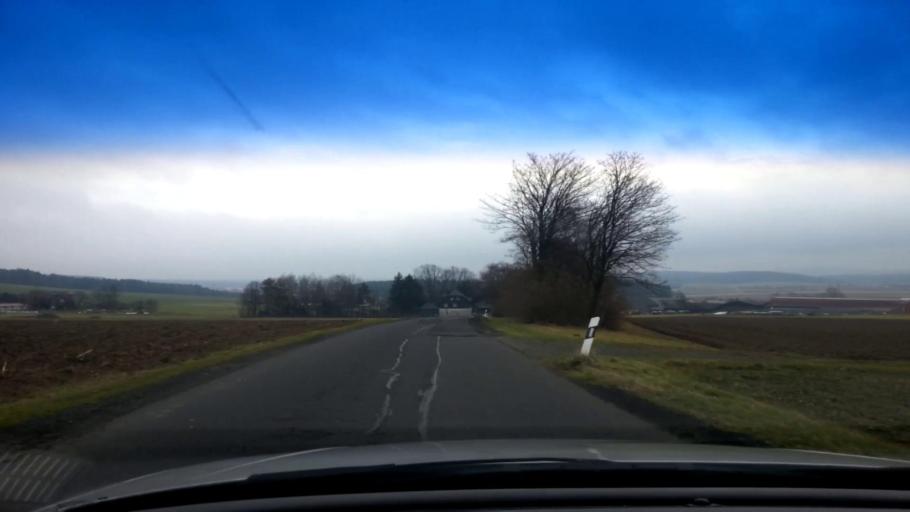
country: DE
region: Bavaria
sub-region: Upper Franconia
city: Kirchenlamitz
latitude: 50.1343
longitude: 11.9300
